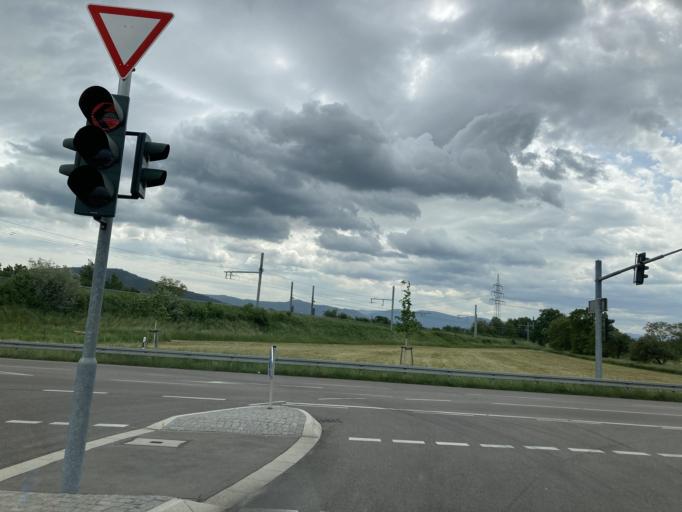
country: DE
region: Baden-Wuerttemberg
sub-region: Karlsruhe Region
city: Muggensturm
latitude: 48.8528
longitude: 8.2650
